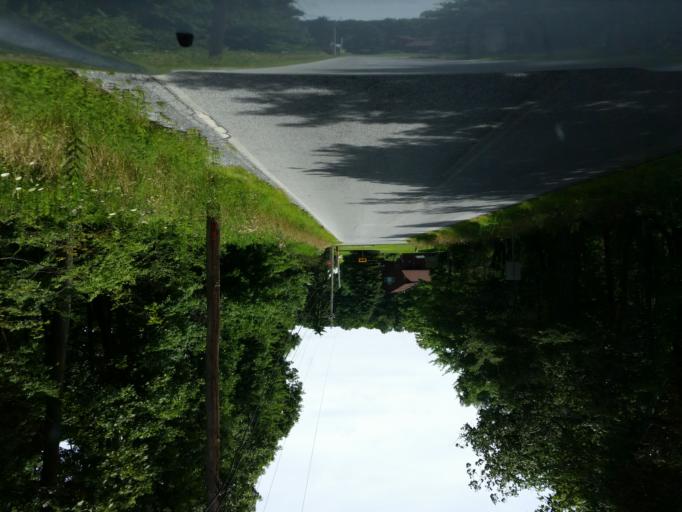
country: US
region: Pennsylvania
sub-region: Blair County
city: Altoona
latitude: 40.5678
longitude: -78.4503
